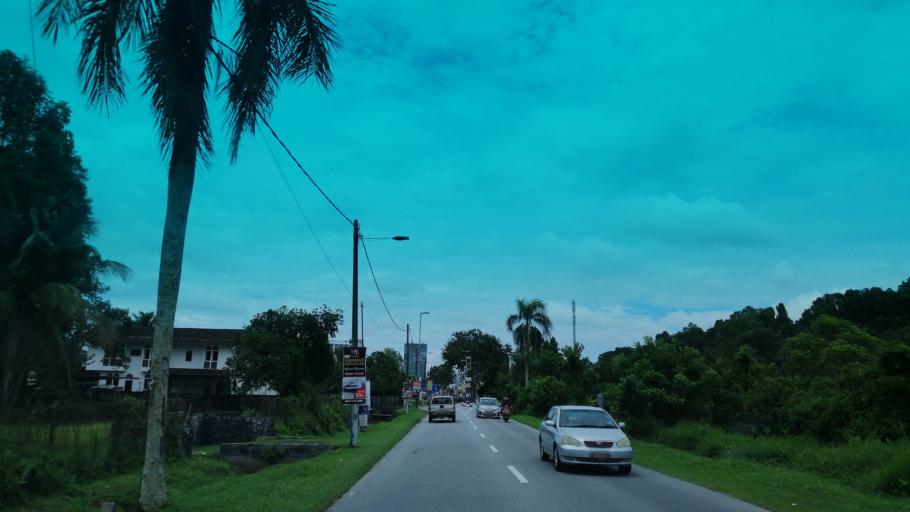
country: MY
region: Perak
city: Taiping
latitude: 4.8627
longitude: 100.7345
